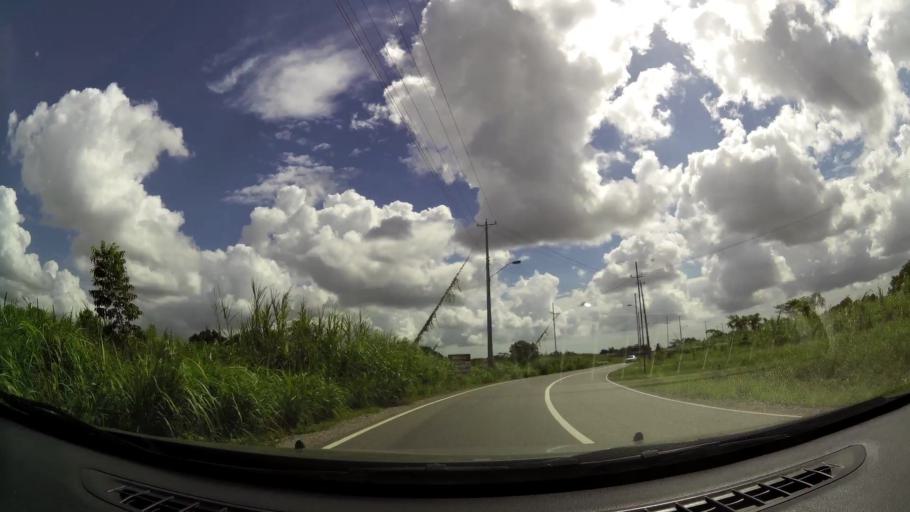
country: TT
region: Penal/Debe
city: Debe
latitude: 10.2295
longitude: -61.4805
